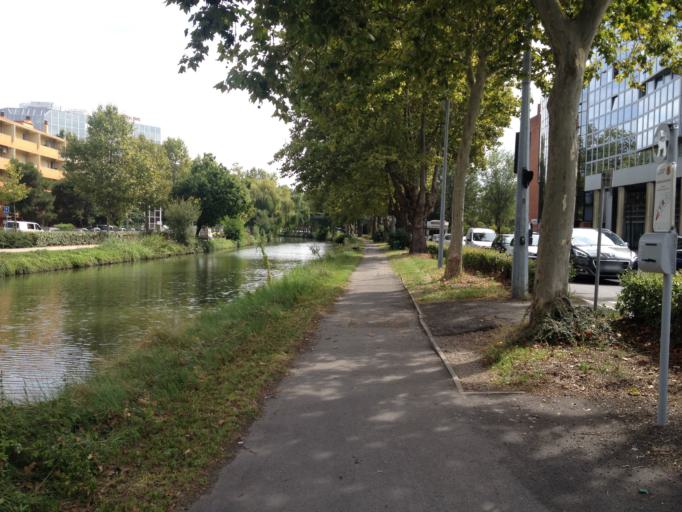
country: FR
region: Midi-Pyrenees
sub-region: Departement de la Haute-Garonne
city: Toulouse
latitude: 43.6127
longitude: 1.4285
